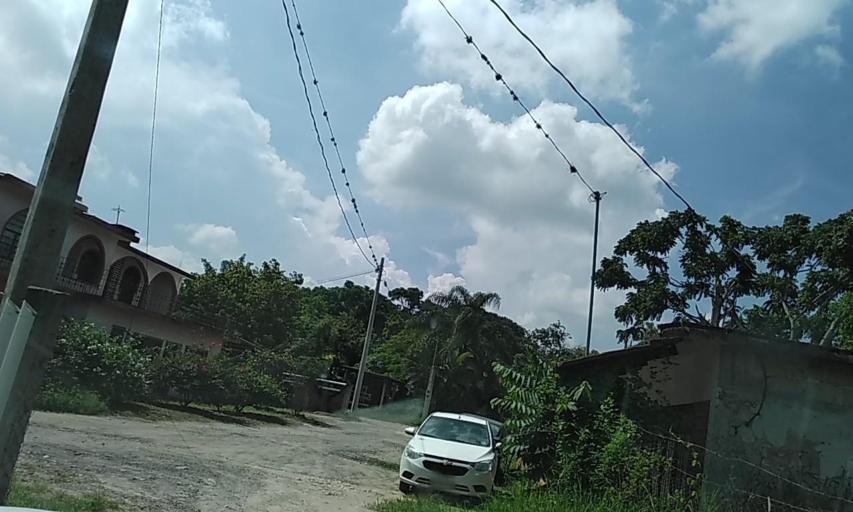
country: MX
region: Veracruz
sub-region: Emiliano Zapata
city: Dos Rios
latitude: 19.4430
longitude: -96.7826
